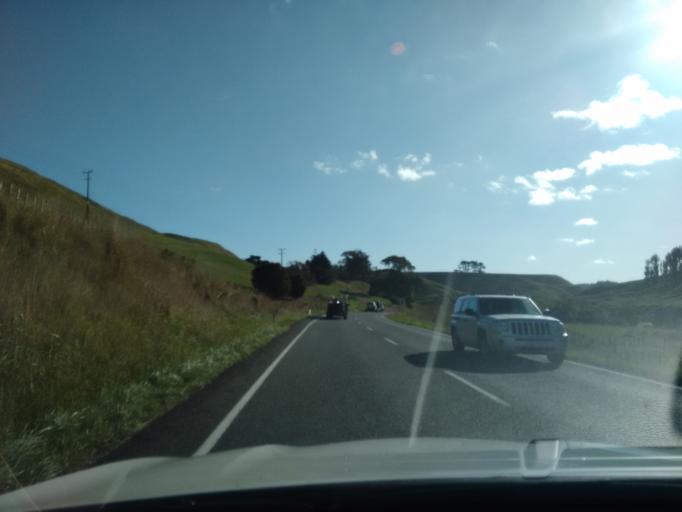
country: NZ
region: Manawatu-Wanganui
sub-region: Wanganui District
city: Wanganui
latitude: -39.8545
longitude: 174.9419
